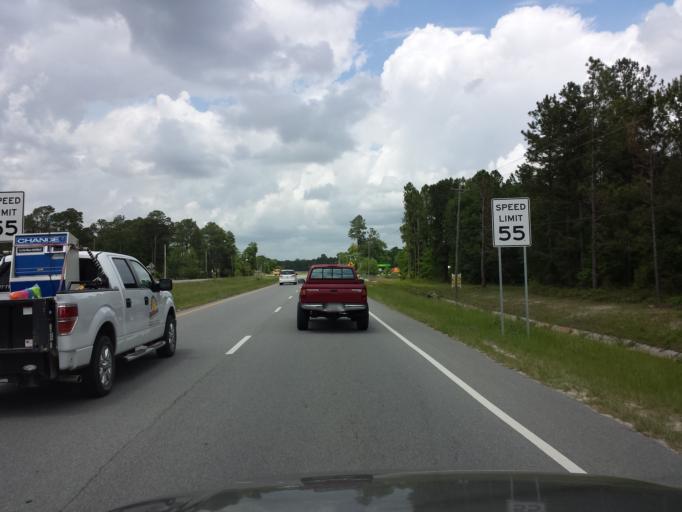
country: US
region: Georgia
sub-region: Lowndes County
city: Valdosta
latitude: 30.7816
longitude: -83.2328
